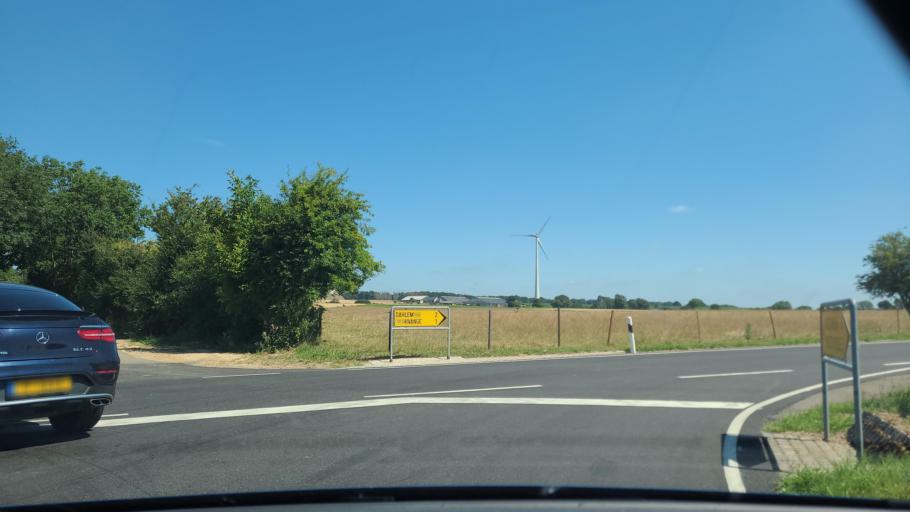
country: LU
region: Luxembourg
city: Hautcharage
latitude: 49.6034
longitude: 5.9179
